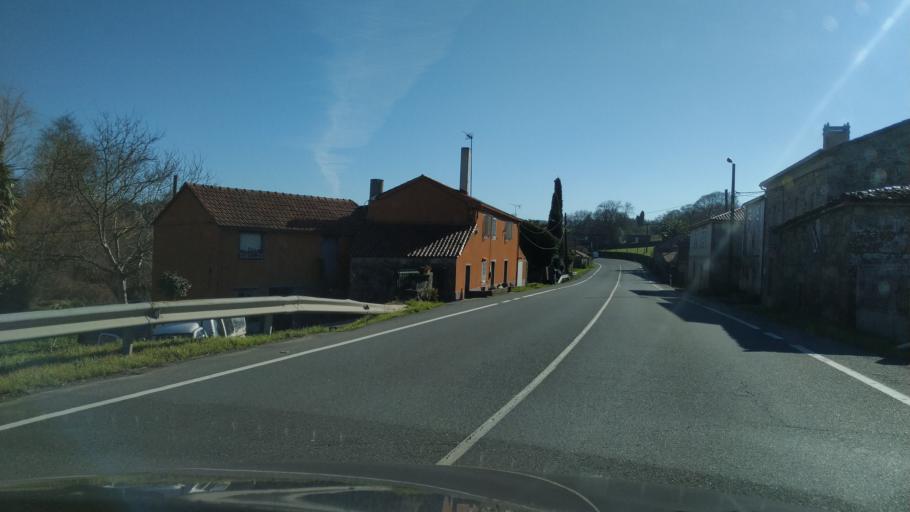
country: ES
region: Galicia
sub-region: Provincia de Pontevedra
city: Silleda
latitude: 42.7237
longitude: -8.2958
